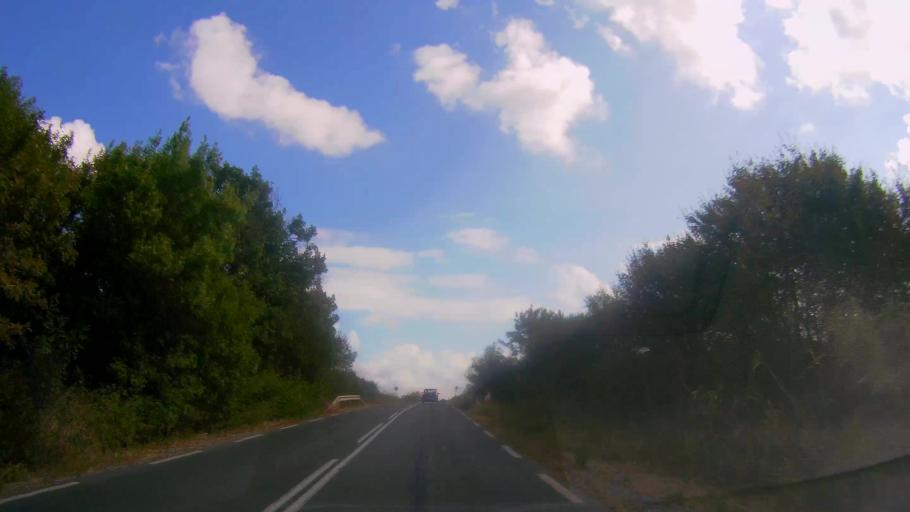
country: BG
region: Burgas
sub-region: Obshtina Kameno
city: Kameno
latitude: 42.4835
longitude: 27.3438
